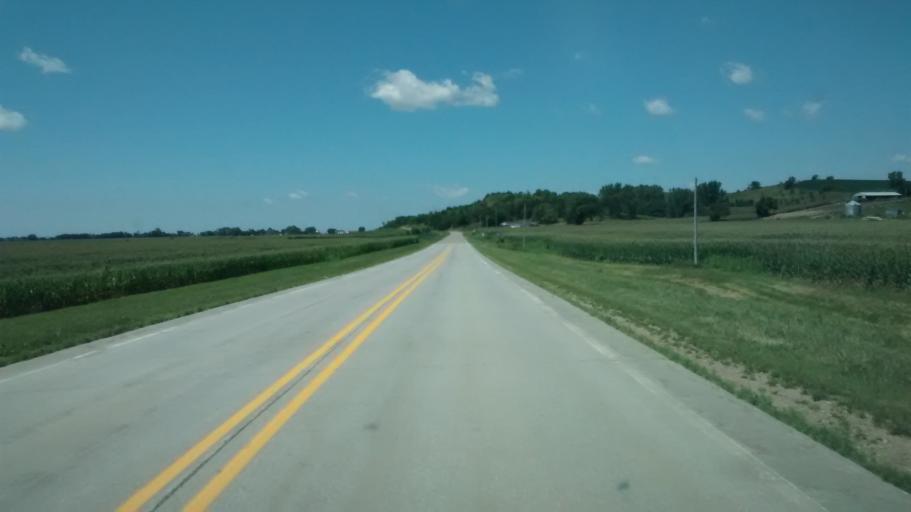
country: US
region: Iowa
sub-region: Woodbury County
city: Moville
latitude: 42.2651
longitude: -96.0548
